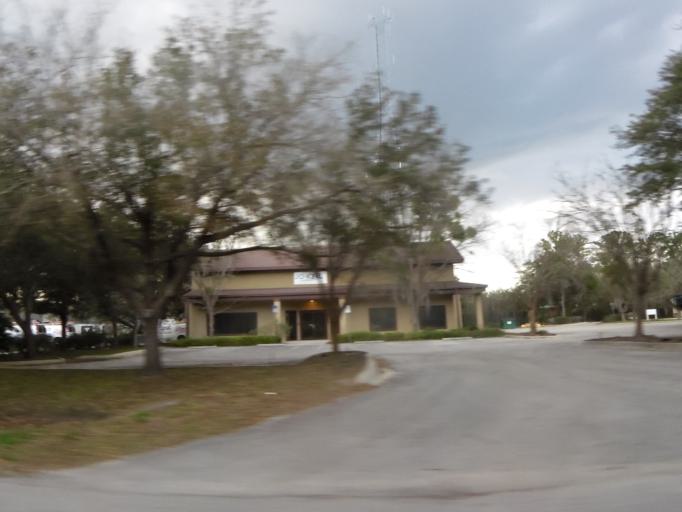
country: US
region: Florida
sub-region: Saint Johns County
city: Fruit Cove
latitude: 30.1843
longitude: -81.5674
